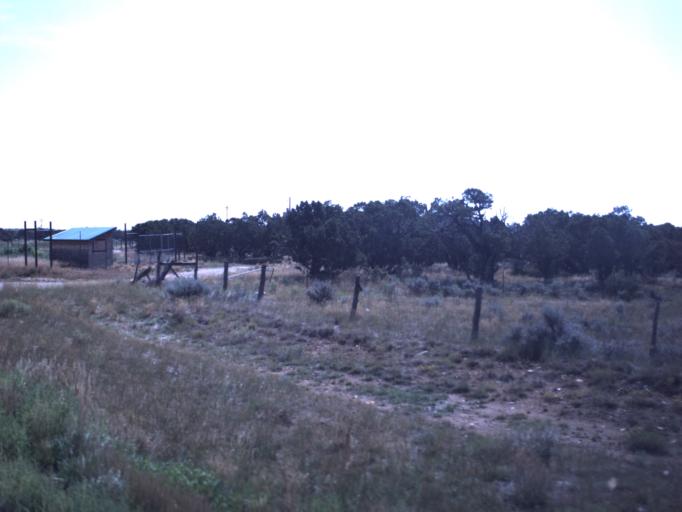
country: US
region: Utah
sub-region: Duchesne County
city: Duchesne
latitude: 40.3498
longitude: -110.4030
